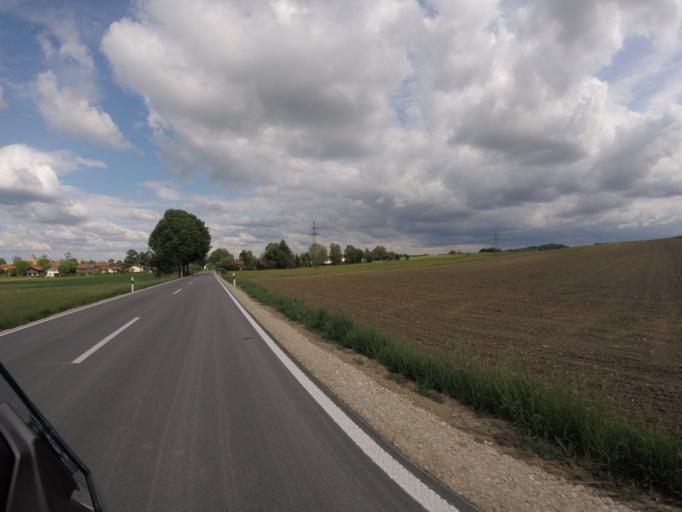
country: DE
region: Bavaria
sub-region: Upper Bavaria
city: Strasslach-Dingharting
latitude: 47.9801
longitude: 11.5144
